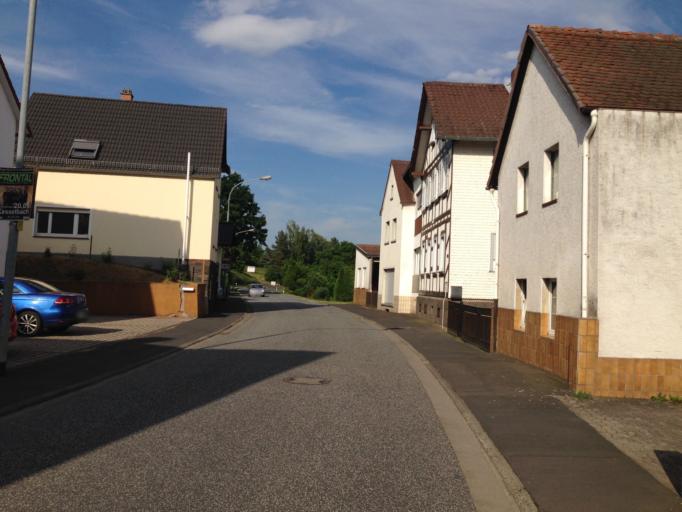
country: DE
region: Hesse
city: Staufenberg
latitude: 50.6618
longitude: 8.7461
